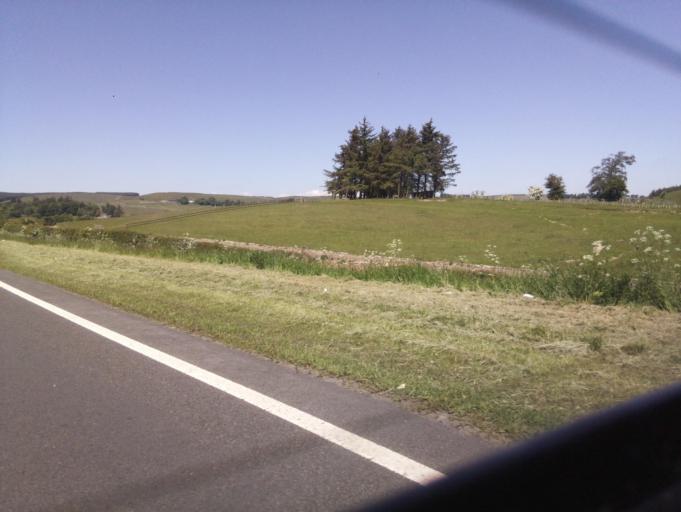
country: GB
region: Scotland
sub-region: The Scottish Borders
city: Selkirk
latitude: 55.4835
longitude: -2.8317
